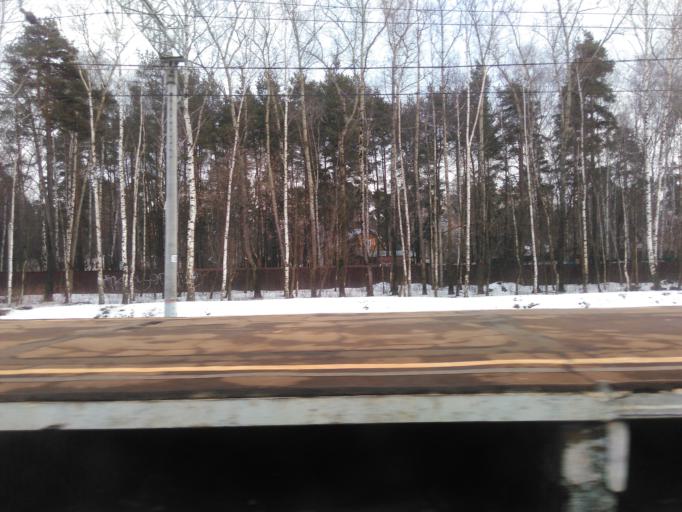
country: RU
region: Moskovskaya
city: Cherkizovo
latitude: 55.9337
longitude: 37.7840
